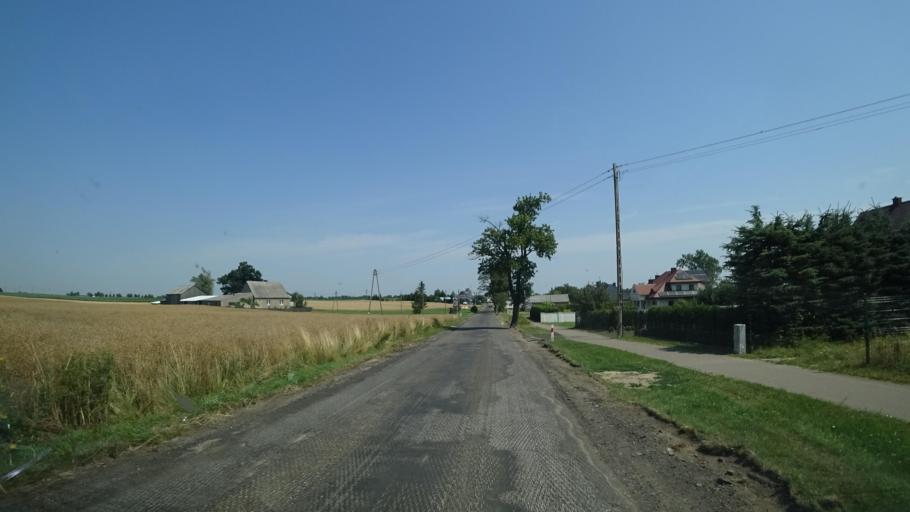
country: PL
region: Pomeranian Voivodeship
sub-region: Powiat chojnicki
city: Brusy
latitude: 53.8771
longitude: 17.6893
